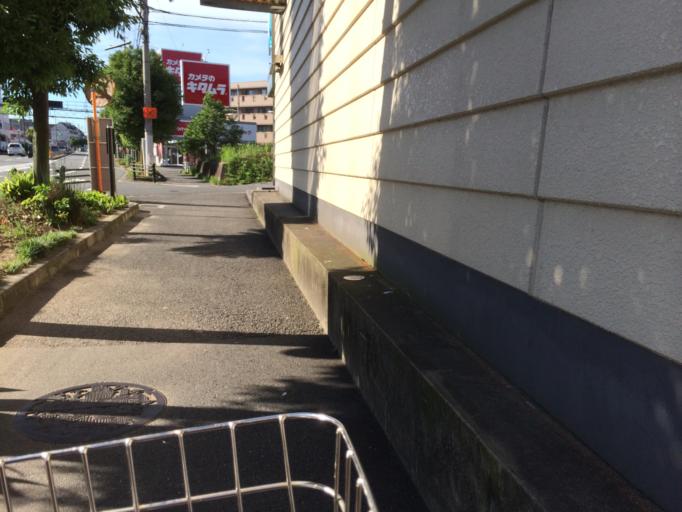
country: JP
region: Nara
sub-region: Ikoma-shi
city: Ikoma
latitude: 34.6984
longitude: 135.7092
